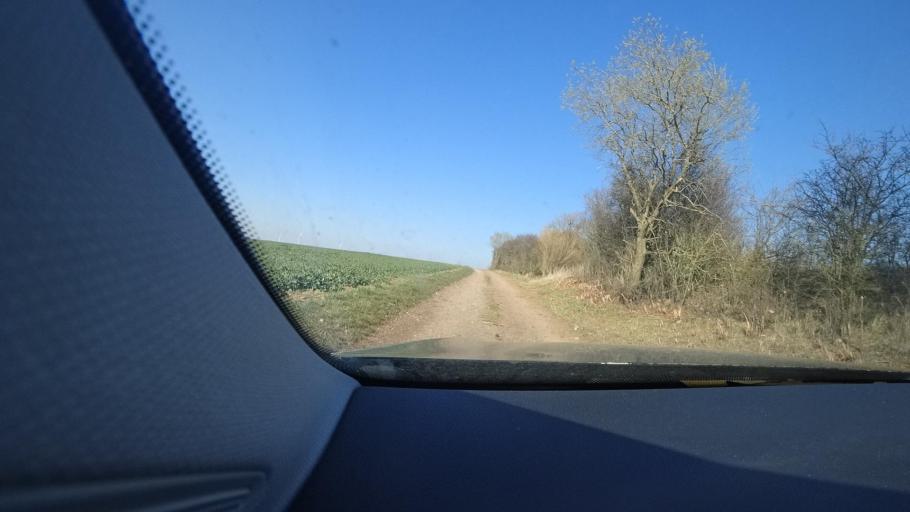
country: DE
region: Rheinland-Pfalz
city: Morschbach
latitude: 50.0047
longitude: 7.6215
